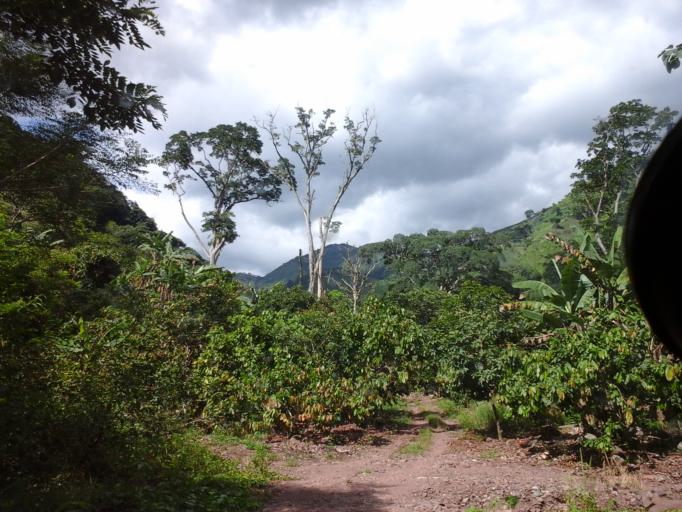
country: CO
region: Cesar
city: San Diego
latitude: 10.2880
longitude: -73.0848
